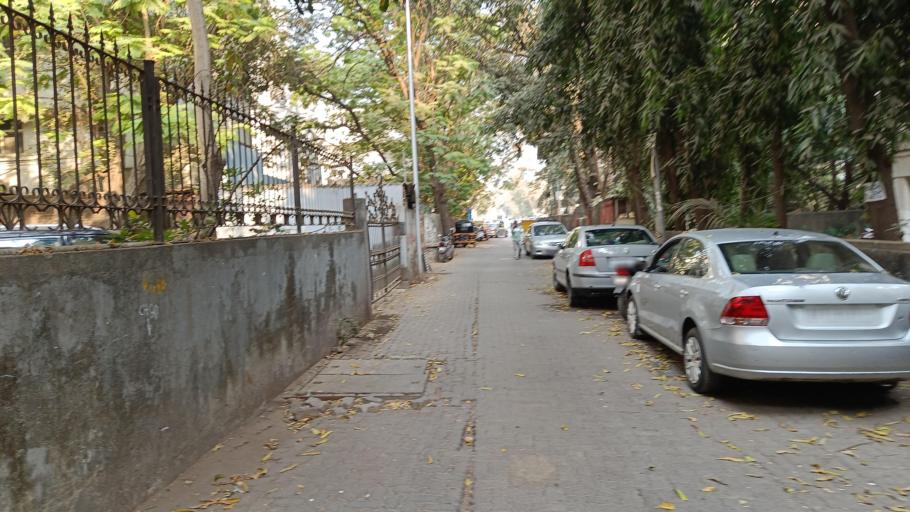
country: IN
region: Maharashtra
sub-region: Mumbai Suburban
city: Mumbai
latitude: 19.0830
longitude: 72.8367
